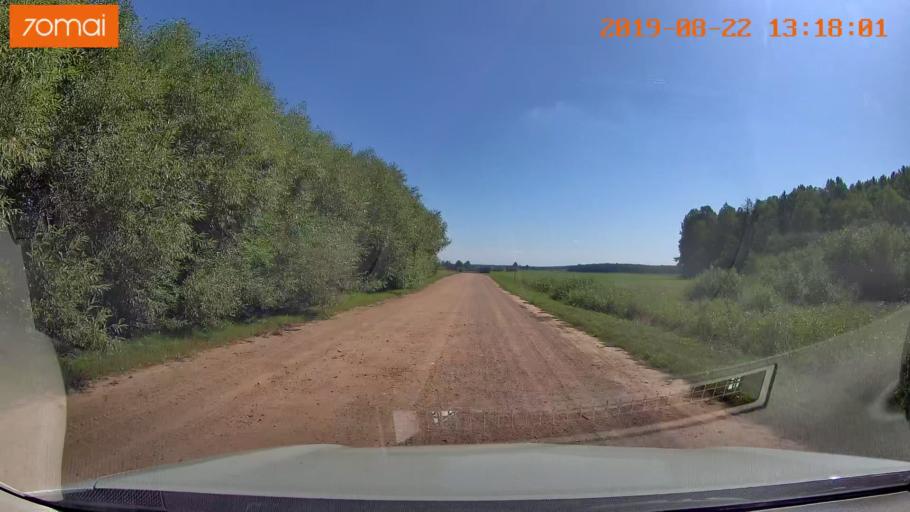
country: BY
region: Minsk
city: Urechcha
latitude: 53.2433
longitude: 27.9314
